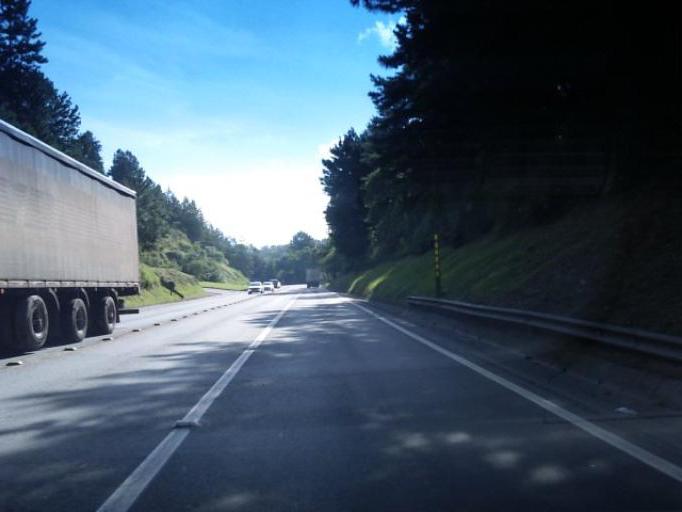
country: BR
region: Parana
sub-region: Campina Grande Do Sul
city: Campina Grande do Sul
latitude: -25.1824
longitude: -48.8837
